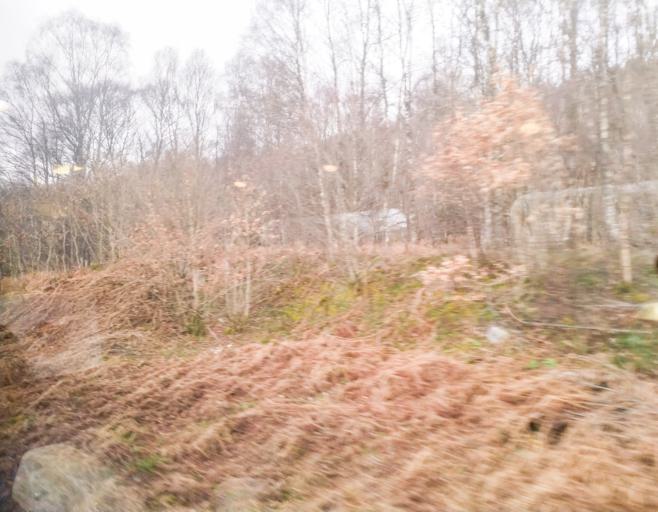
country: GB
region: Scotland
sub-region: Highland
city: Spean Bridge
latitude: 56.8853
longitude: -4.8162
